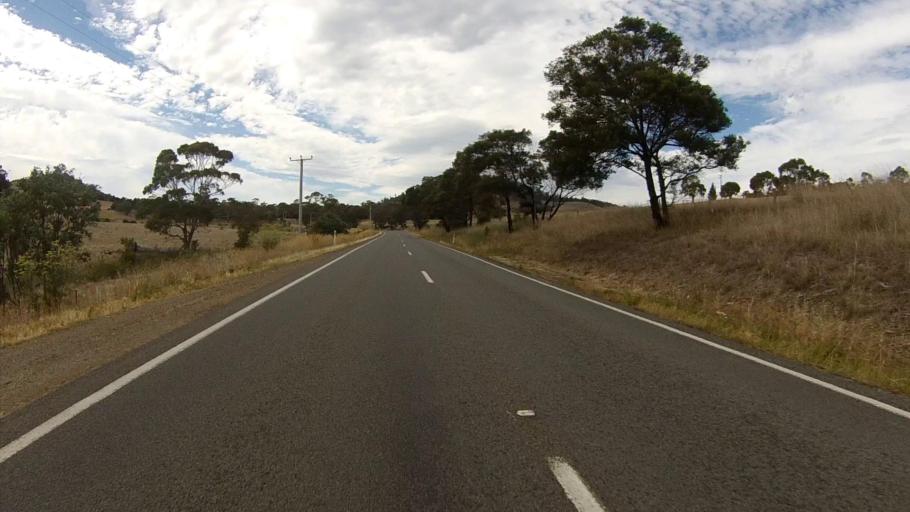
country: AU
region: Tasmania
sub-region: Sorell
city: Sorell
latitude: -42.6983
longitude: 147.4841
